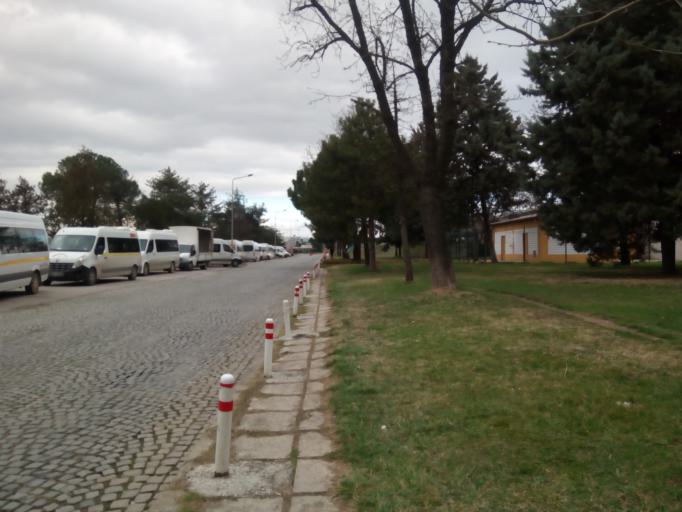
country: TR
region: Bursa
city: Niluefer
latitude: 40.2485
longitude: 28.9594
